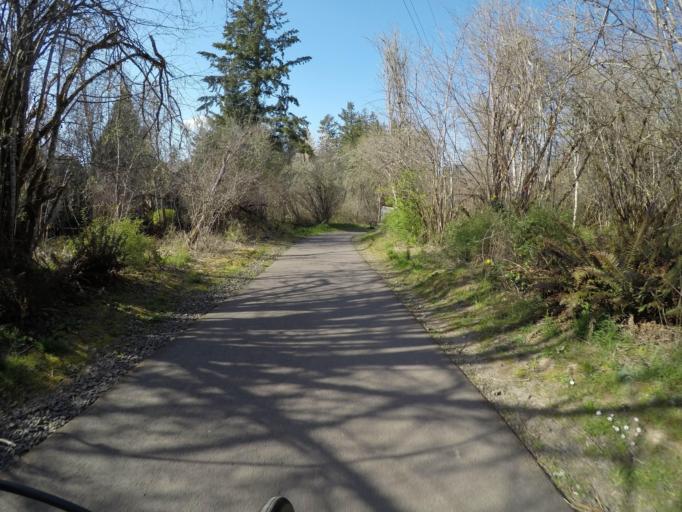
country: US
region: Oregon
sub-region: Washington County
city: Oak Hills
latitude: 45.5546
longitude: -122.8468
